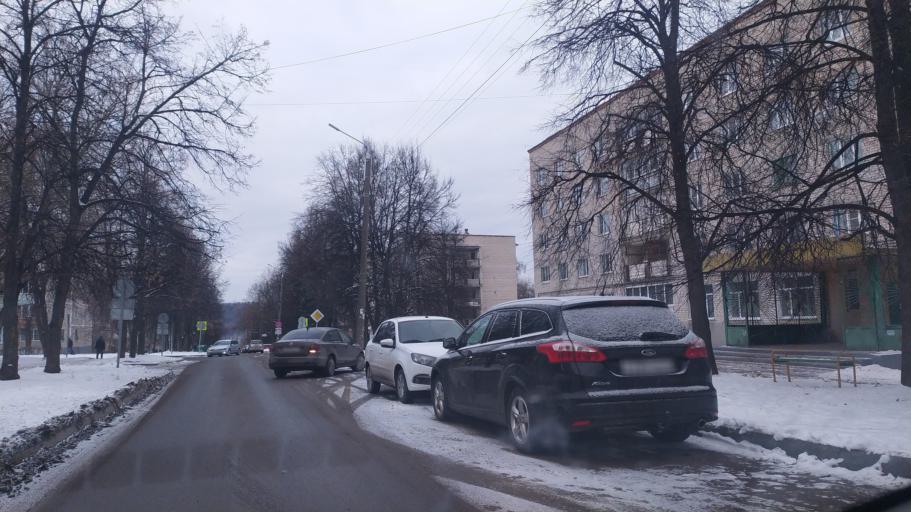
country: RU
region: Chuvashia
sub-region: Cheboksarskiy Rayon
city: Cheboksary
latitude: 56.1244
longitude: 47.1992
